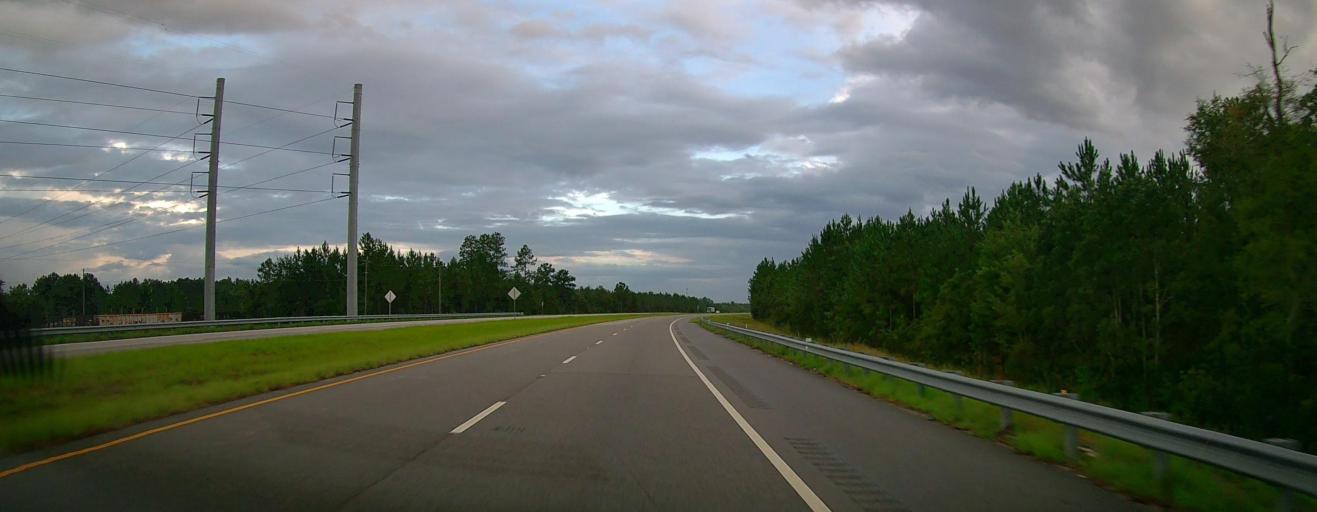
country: US
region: Georgia
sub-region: Ware County
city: Deenwood
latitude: 31.1687
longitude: -82.4118
